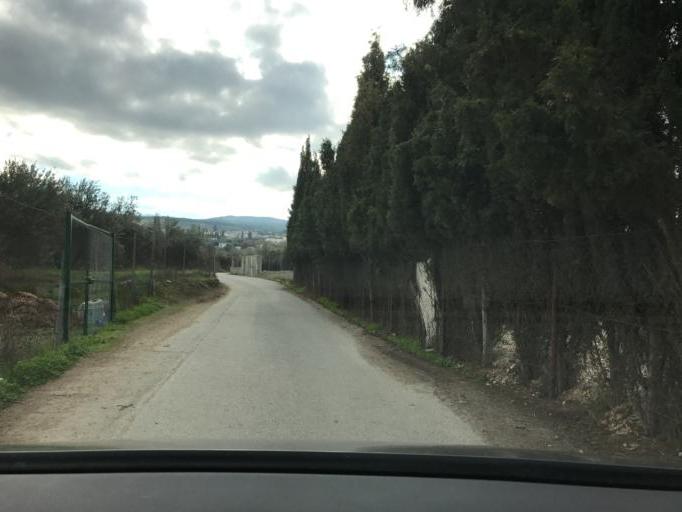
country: ES
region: Andalusia
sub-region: Provincia de Granada
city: Cajar
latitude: 37.1299
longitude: -3.5795
